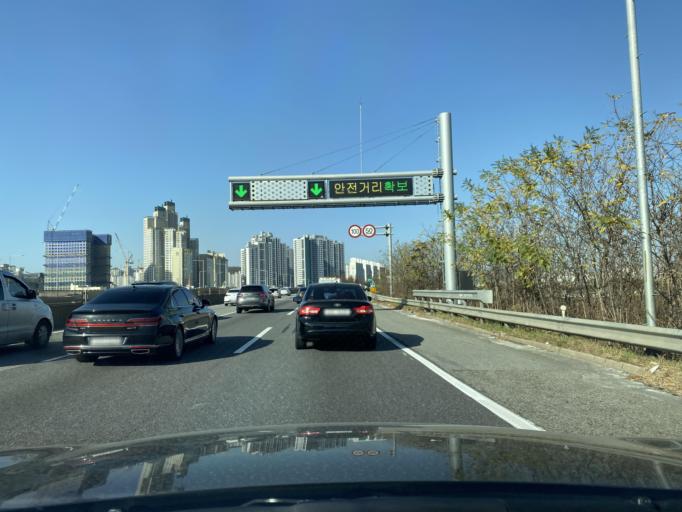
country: KR
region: Incheon
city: Incheon
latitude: 37.3966
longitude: 126.7430
